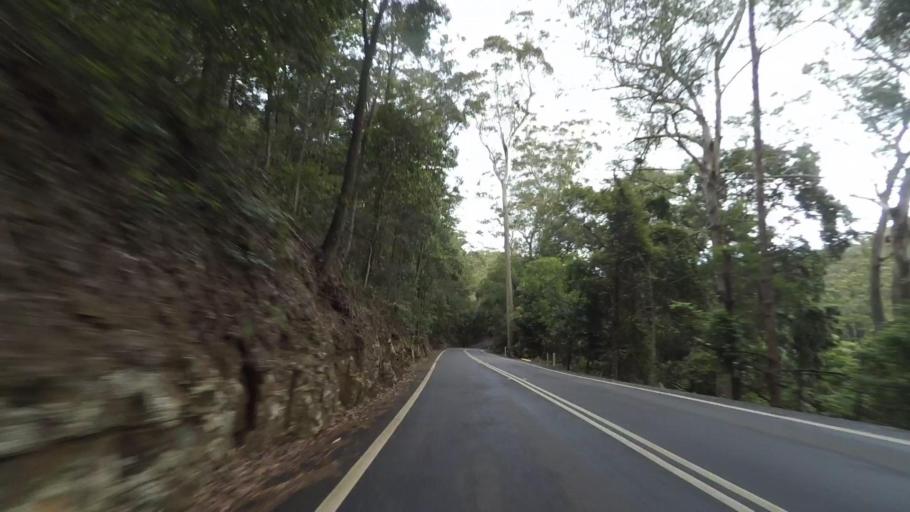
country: AU
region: New South Wales
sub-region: Wollongong
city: Helensburgh
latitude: -34.1648
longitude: 151.0158
